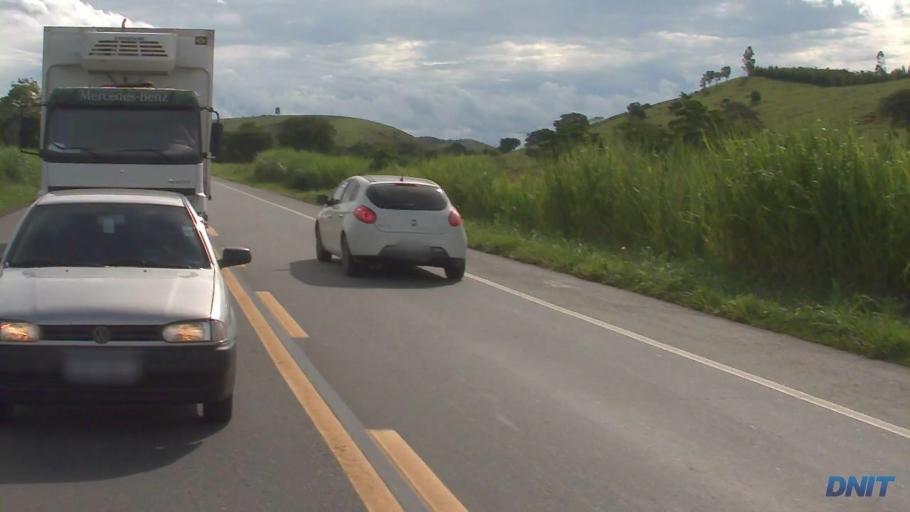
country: BR
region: Minas Gerais
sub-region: Belo Oriente
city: Belo Oriente
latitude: -19.2086
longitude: -42.3023
